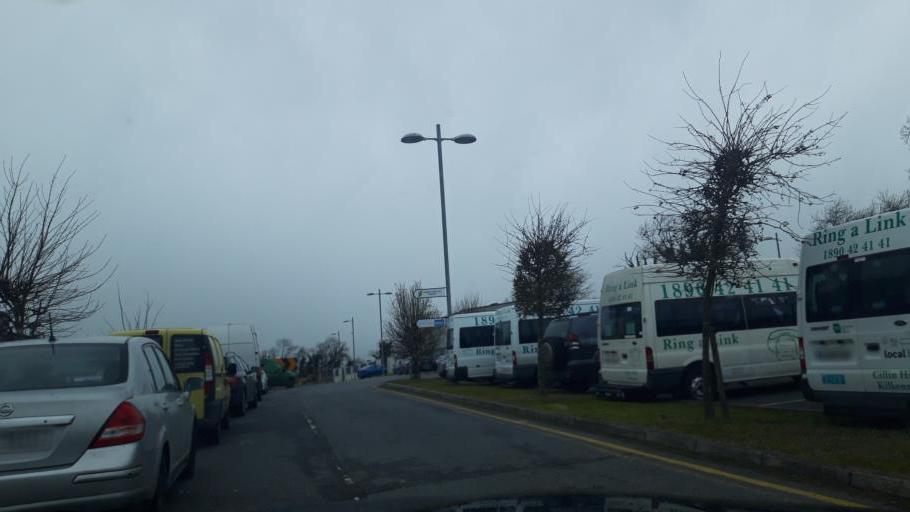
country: IE
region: Leinster
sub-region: Kilkenny
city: Kilkenny
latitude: 52.6509
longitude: -7.2097
